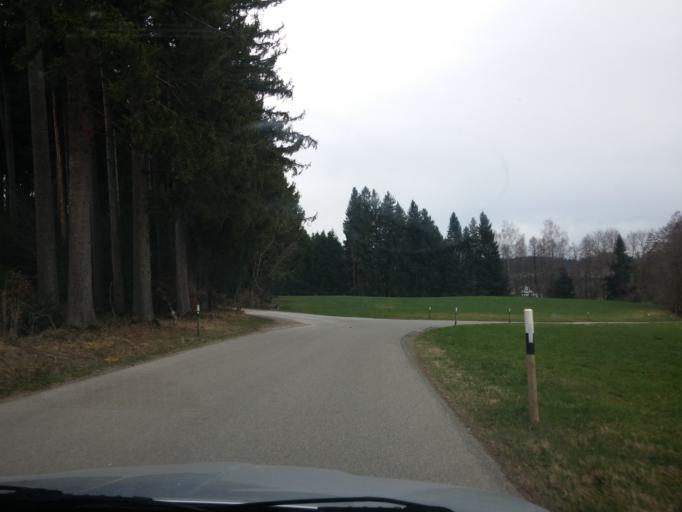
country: DE
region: Bavaria
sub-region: Swabia
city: Woringen
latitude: 47.9125
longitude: 10.1833
